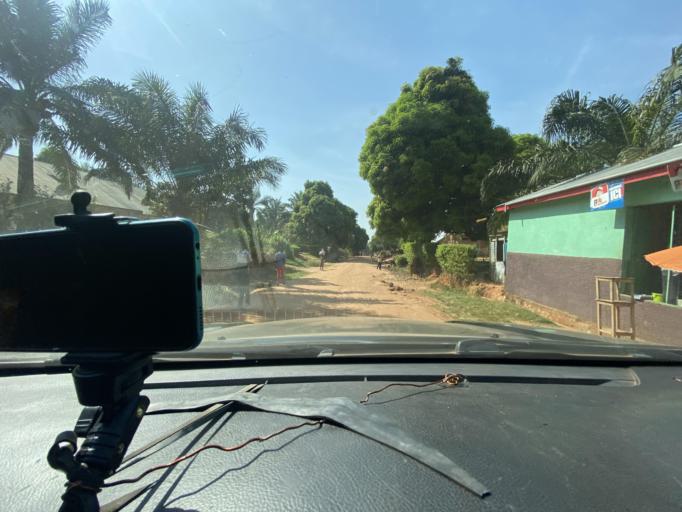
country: CD
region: Kasai-Oriental
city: Kabinda
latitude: -6.1282
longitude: 24.5015
